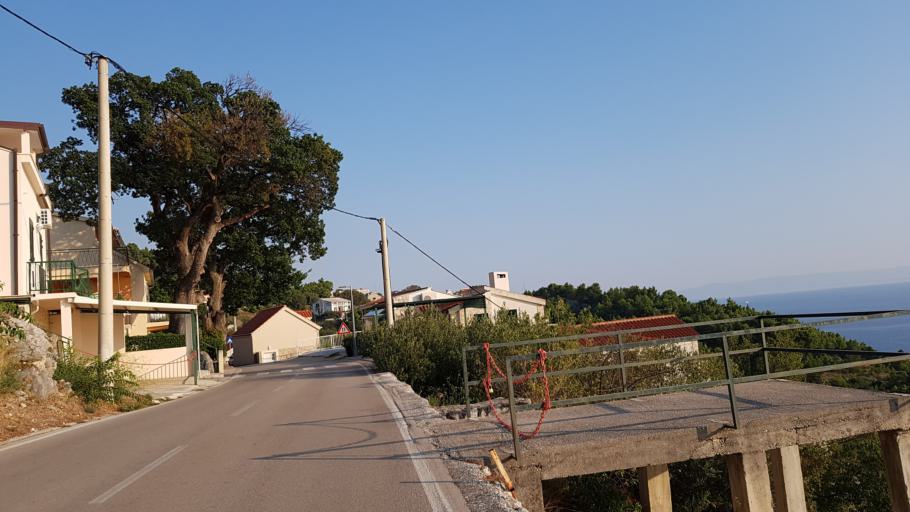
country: HR
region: Splitsko-Dalmatinska
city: Donja Brela
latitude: 43.3800
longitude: 16.9197
